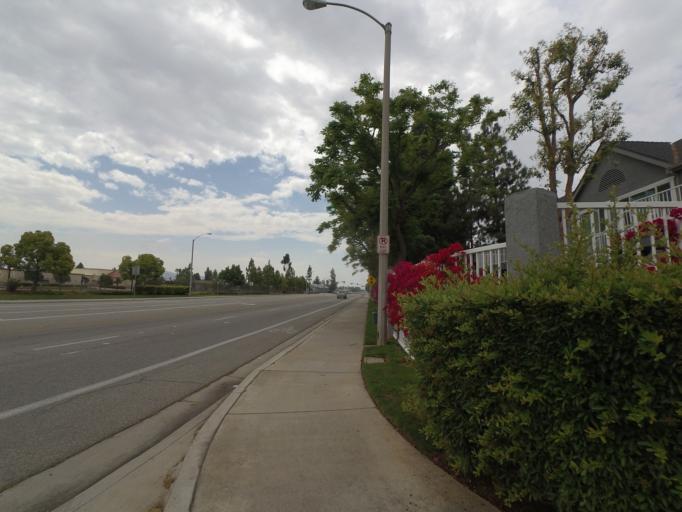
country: US
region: California
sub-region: Riverside County
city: Moreno Valley
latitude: 33.9299
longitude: -117.2439
